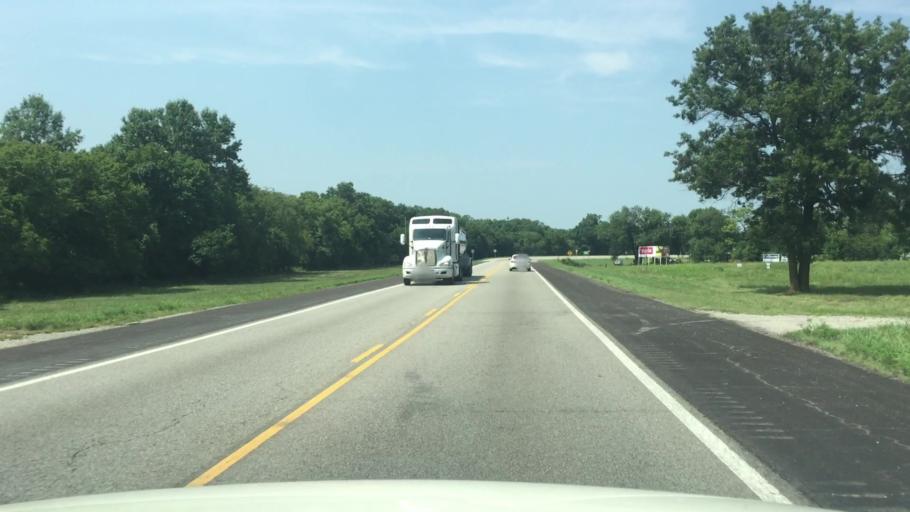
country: US
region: Kansas
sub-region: Crawford County
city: Pittsburg
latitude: 37.4049
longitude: -94.7235
